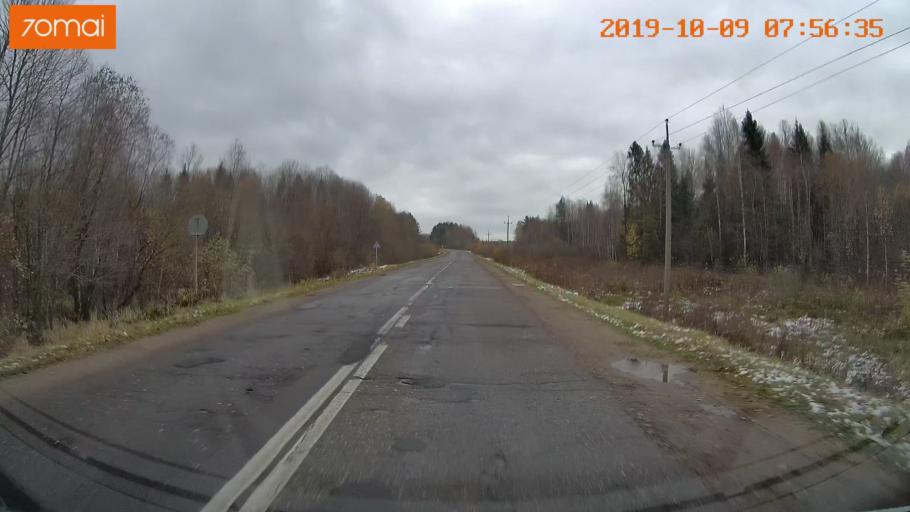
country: RU
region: Jaroslavl
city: Kukoboy
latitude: 58.6977
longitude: 39.9374
